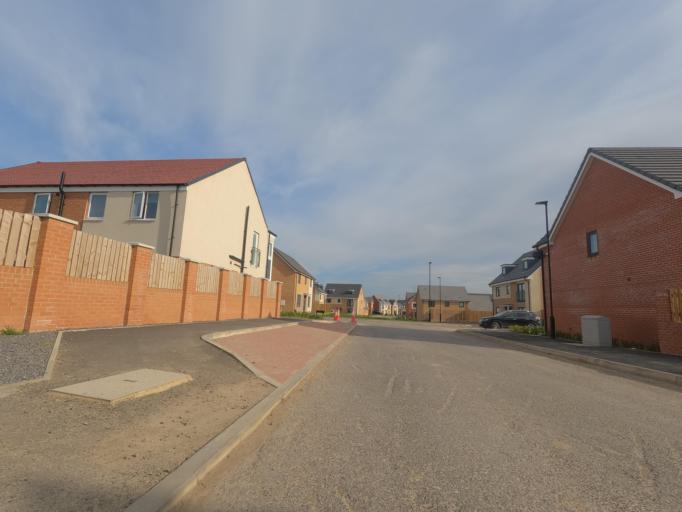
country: GB
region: England
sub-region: Newcastle upon Tyne
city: Hazlerigg
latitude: 55.0304
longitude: -1.6611
